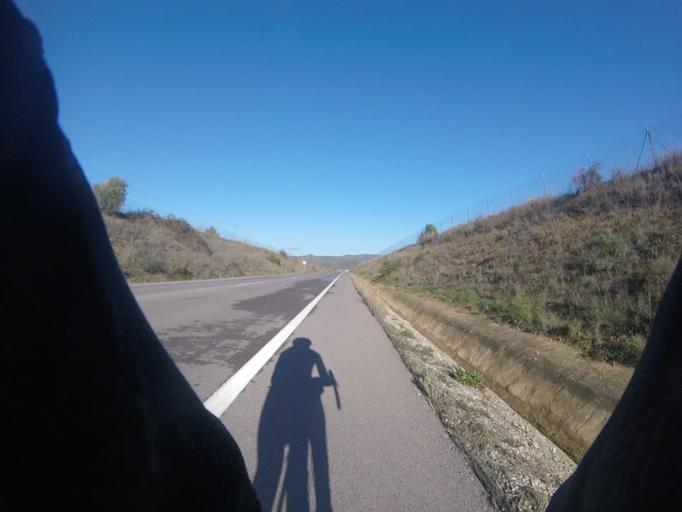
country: ES
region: Valencia
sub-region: Provincia de Castello
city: Cuevas de Vinroma
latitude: 40.3119
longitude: 0.1175
